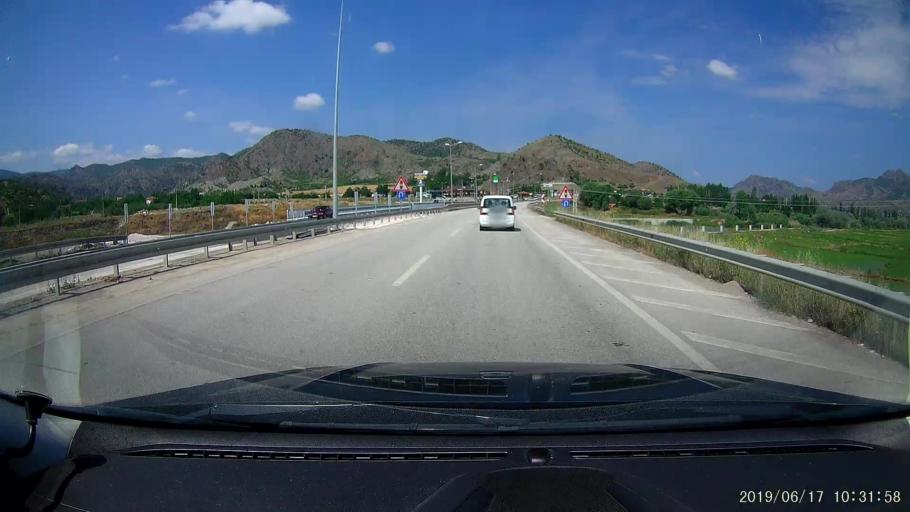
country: TR
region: Corum
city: Osmancik
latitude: 40.9779
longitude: 34.7779
